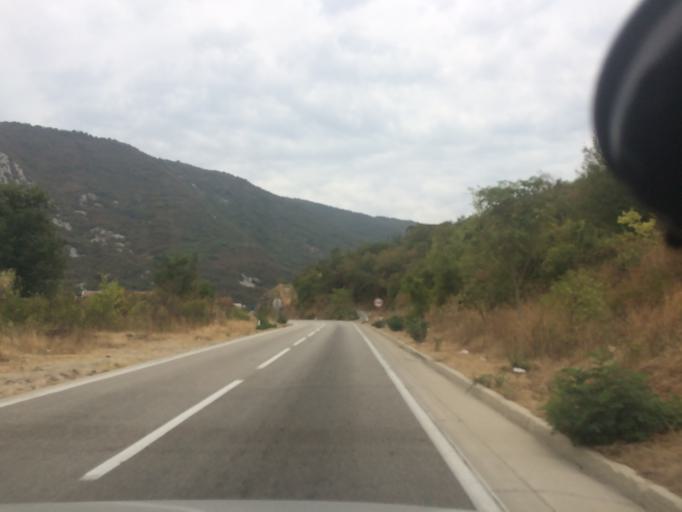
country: ME
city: Lipci
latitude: 42.4927
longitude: 18.6486
